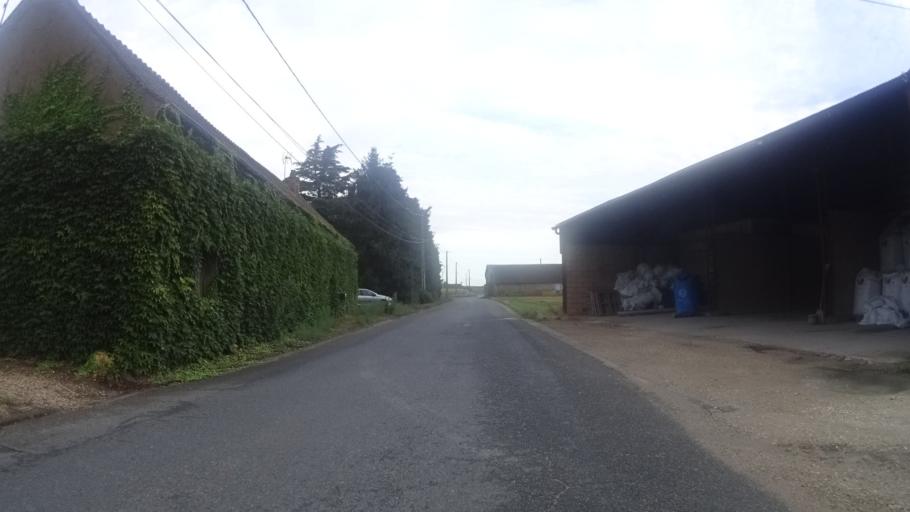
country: FR
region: Centre
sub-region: Departement du Loiret
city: Saint-Benoit-sur-Loire
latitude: 47.7948
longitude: 2.3129
